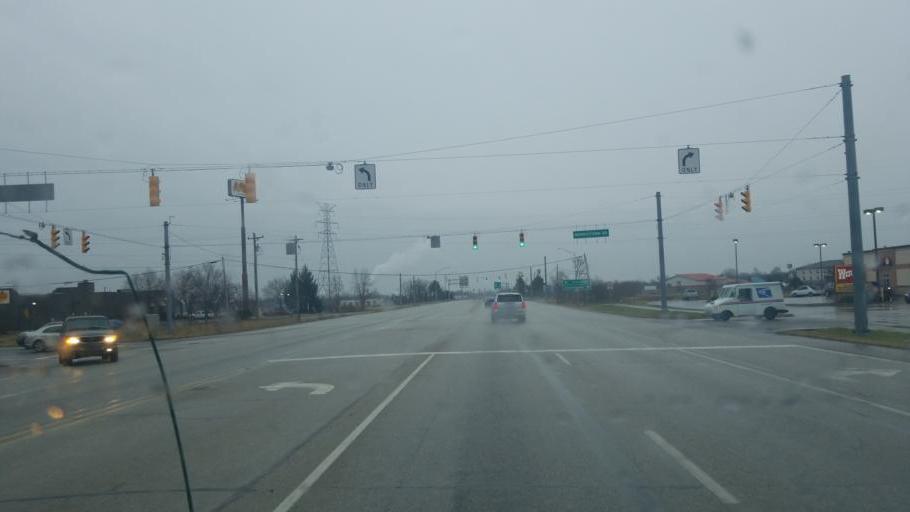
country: US
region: Indiana
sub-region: Shelby County
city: Shelbyville
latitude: 39.5543
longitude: -85.7758
